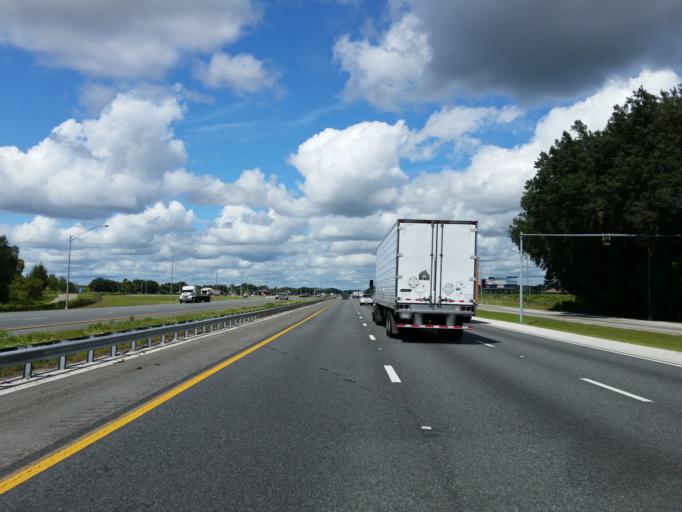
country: US
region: Florida
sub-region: Marion County
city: Belleview
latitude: 28.9883
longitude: -82.1402
